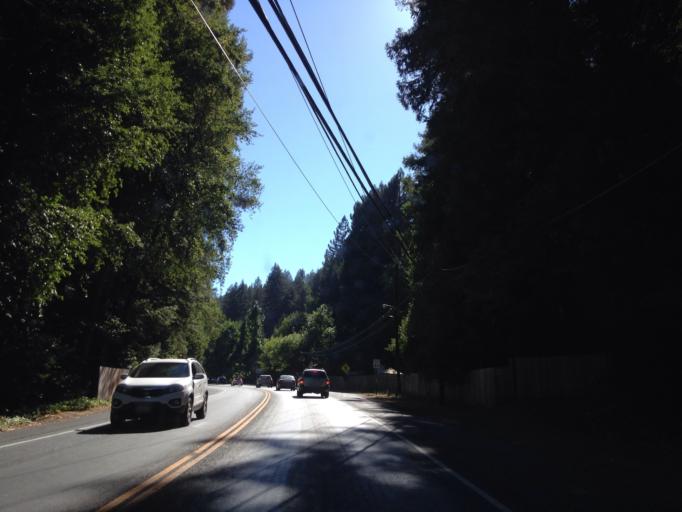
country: US
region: California
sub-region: Sonoma County
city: Guerneville
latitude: 38.5170
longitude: -122.9819
